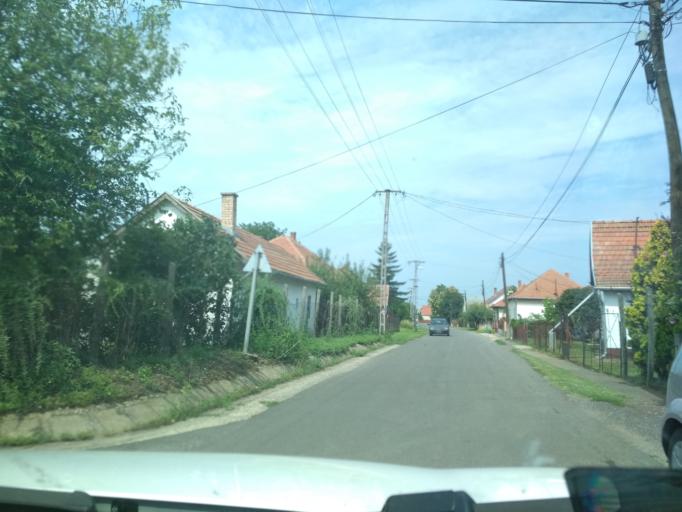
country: HU
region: Jasz-Nagykun-Szolnok
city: Tiszafured
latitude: 47.6087
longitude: 20.7596
